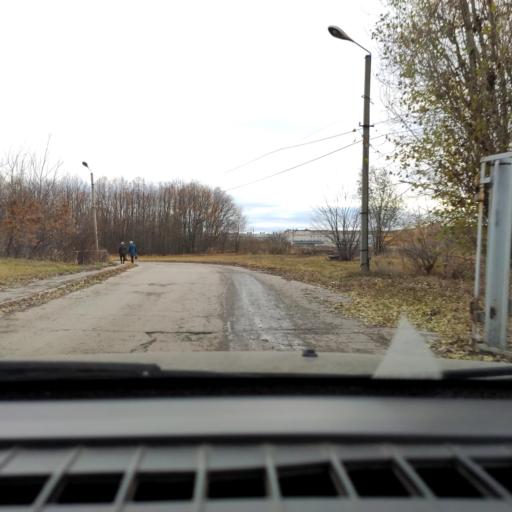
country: RU
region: Samara
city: Tol'yatti
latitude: 53.5441
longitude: 49.2972
